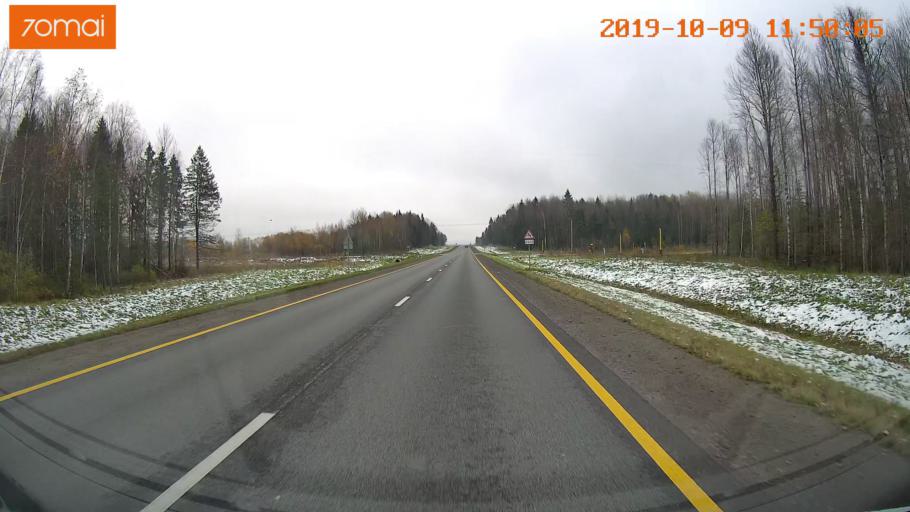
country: RU
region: Vologda
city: Gryazovets
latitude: 58.8101
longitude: 40.2407
